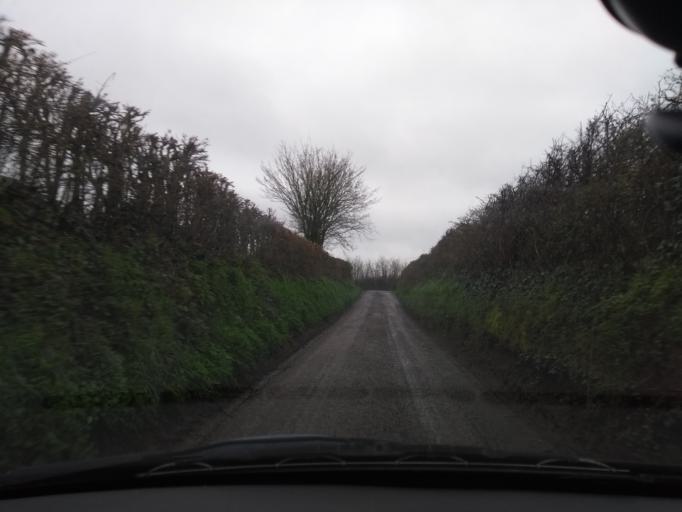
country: GB
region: England
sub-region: Somerset
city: Taunton
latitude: 51.0431
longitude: -3.1210
